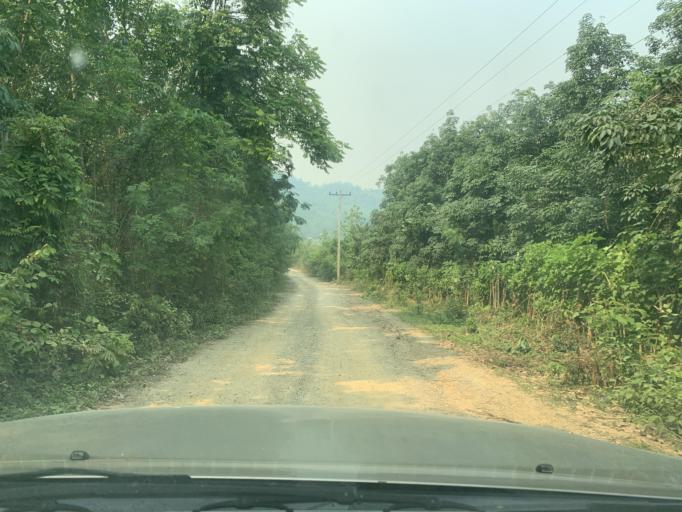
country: LA
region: Louangphabang
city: Louangphabang
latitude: 19.8981
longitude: 102.2546
